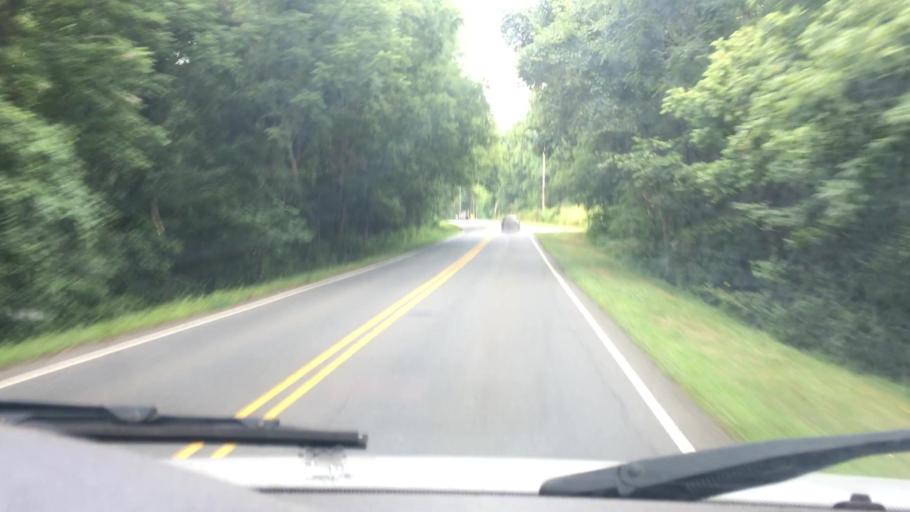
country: US
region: North Carolina
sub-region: Mecklenburg County
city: Huntersville
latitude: 35.4069
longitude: -80.8895
